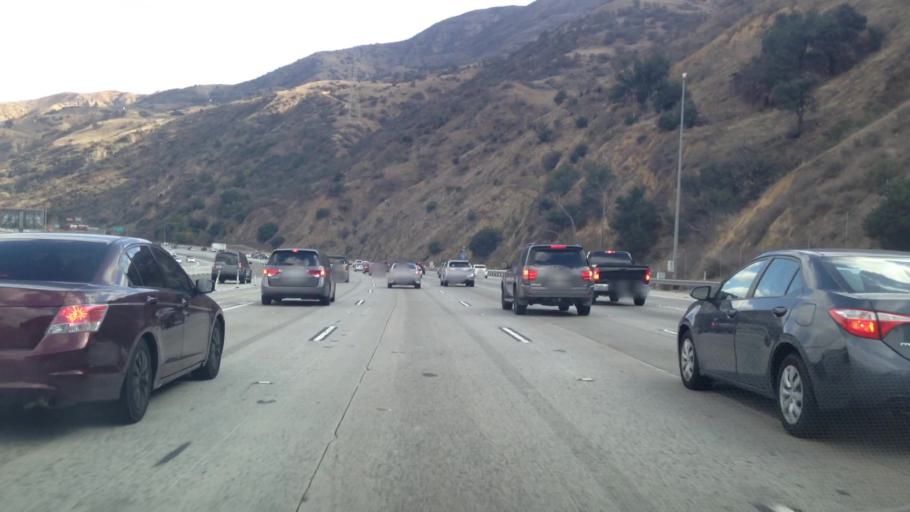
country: US
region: California
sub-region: San Bernardino County
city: Los Serranos
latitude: 33.8696
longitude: -117.6818
